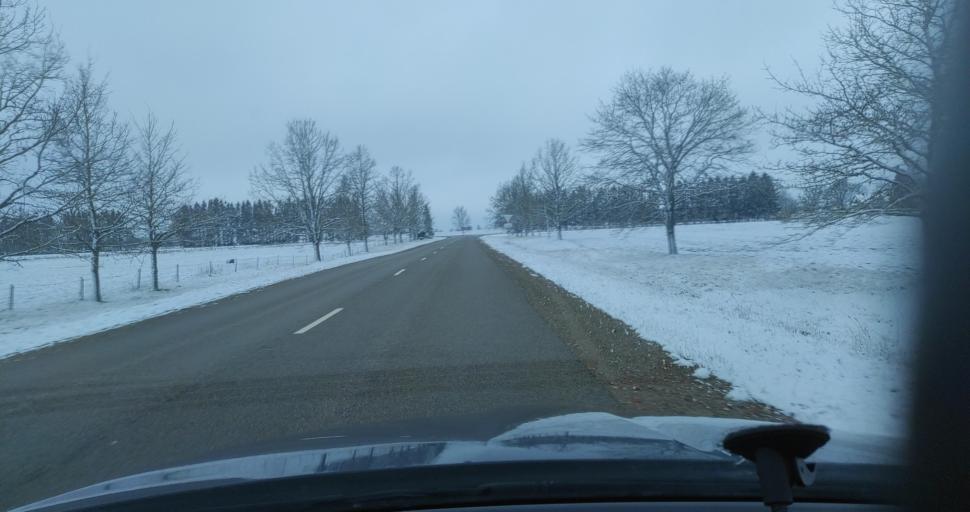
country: LV
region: Skrunda
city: Skrunda
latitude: 56.8473
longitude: 22.2265
